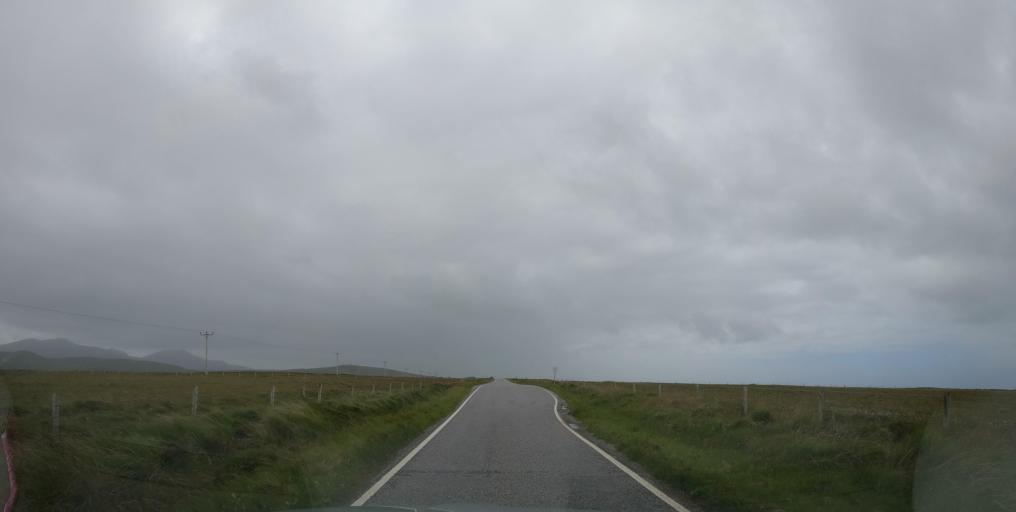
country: GB
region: Scotland
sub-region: Eilean Siar
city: Benbecula
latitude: 57.3702
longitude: -7.3490
